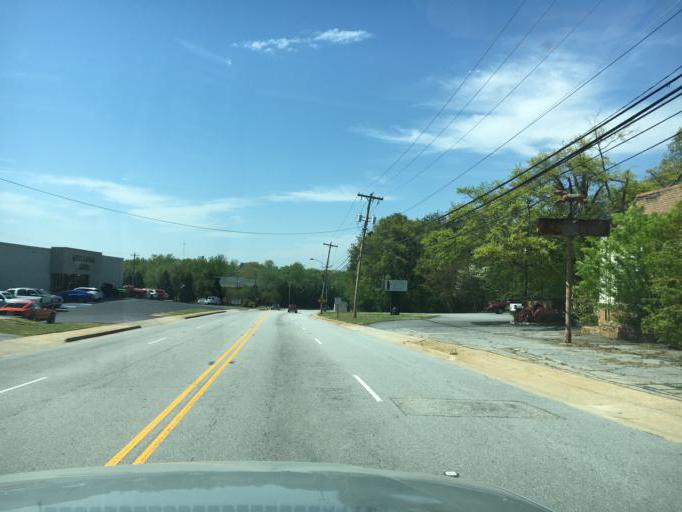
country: US
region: South Carolina
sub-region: Greenville County
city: Greer
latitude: 34.9533
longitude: -82.2272
